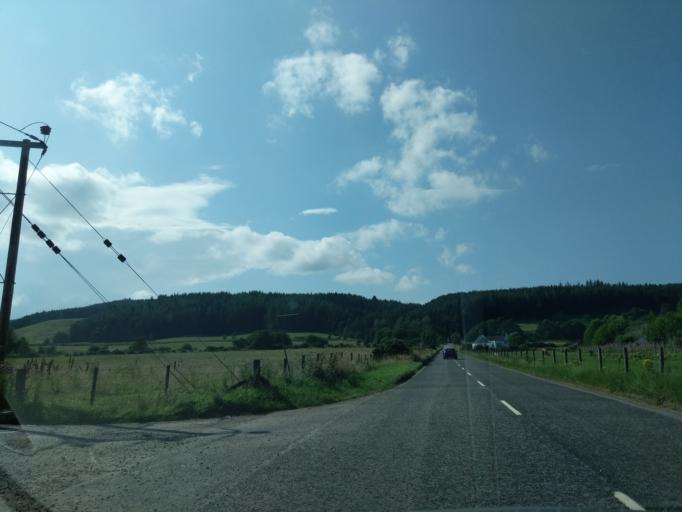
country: GB
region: Scotland
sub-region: Moray
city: Rothes
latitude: 57.5520
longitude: -3.1459
